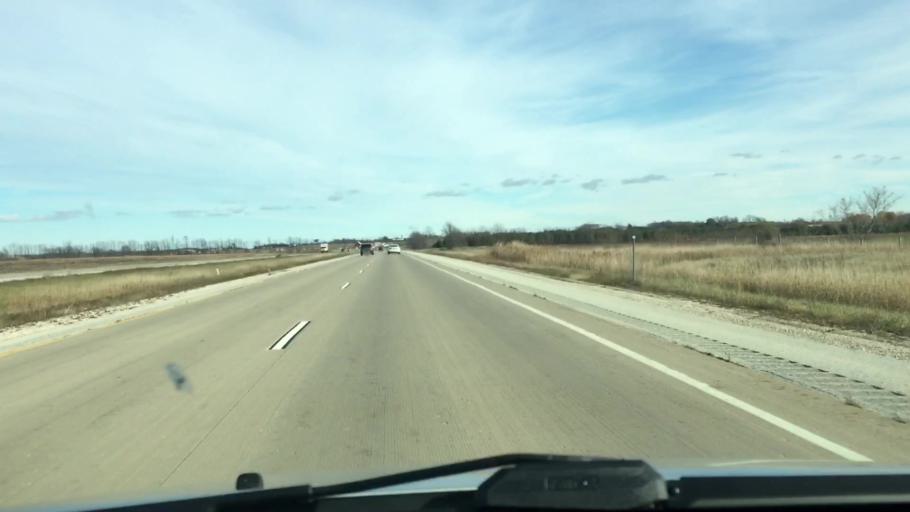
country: US
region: Wisconsin
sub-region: Kewaunee County
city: Luxemburg
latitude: 44.7160
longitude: -87.6409
